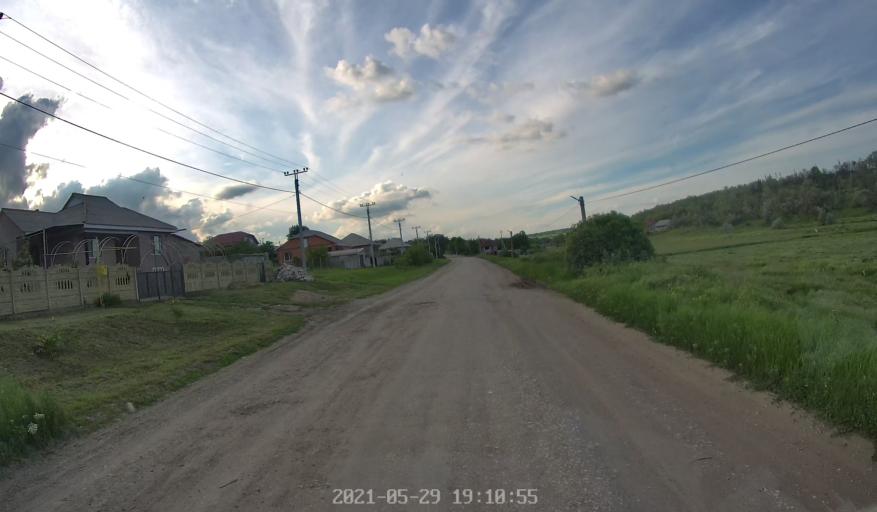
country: MD
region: Chisinau
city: Singera
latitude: 46.8352
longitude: 28.9555
